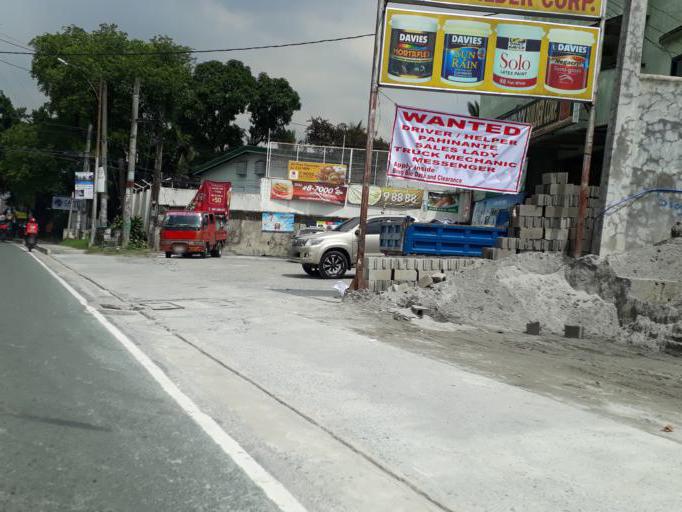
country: PH
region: Calabarzon
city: Bagong Pagasa
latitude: 14.6780
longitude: 121.0300
